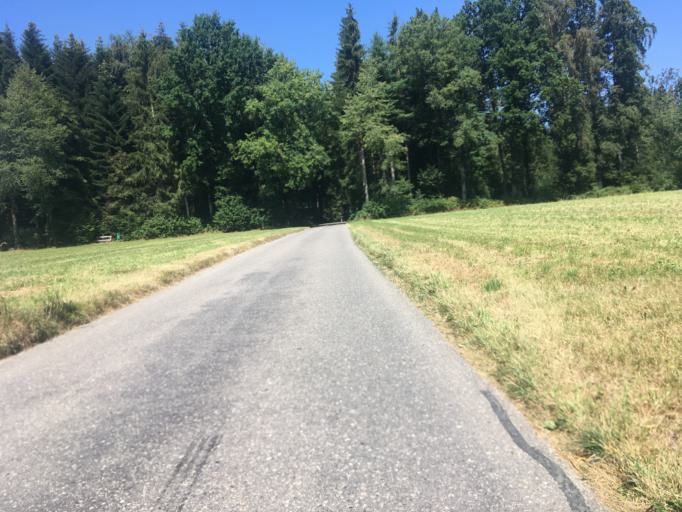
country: CH
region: Bern
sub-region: Bern-Mittelland District
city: Fraubrunnen
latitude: 47.0863
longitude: 7.5098
